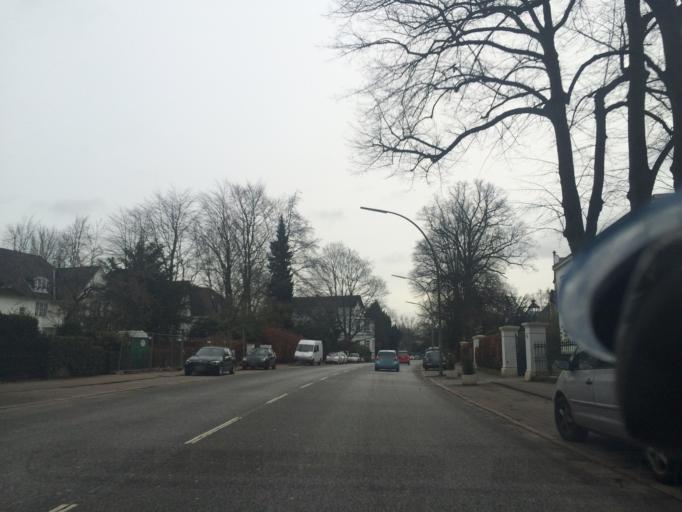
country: DE
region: Hamburg
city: Altona
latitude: 53.5461
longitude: 9.9107
